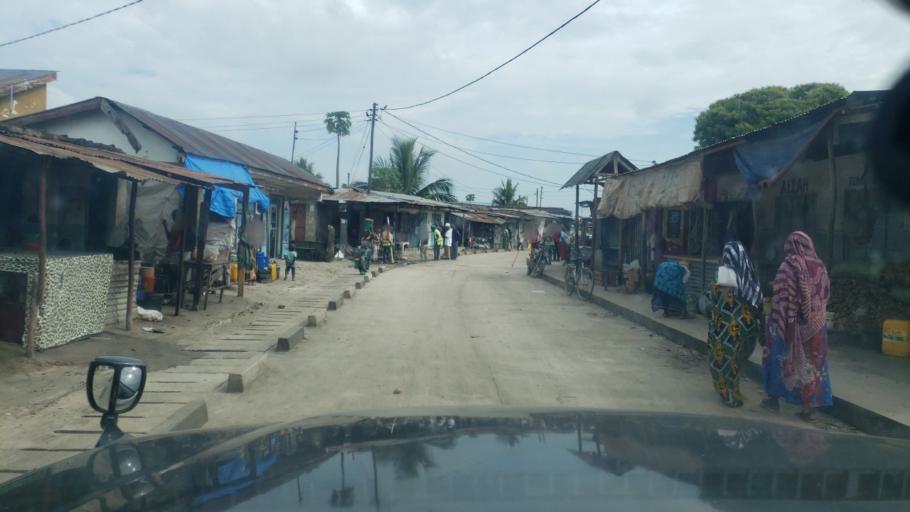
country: TZ
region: Pwani
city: Vikindu
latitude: -6.9260
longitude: 39.2548
